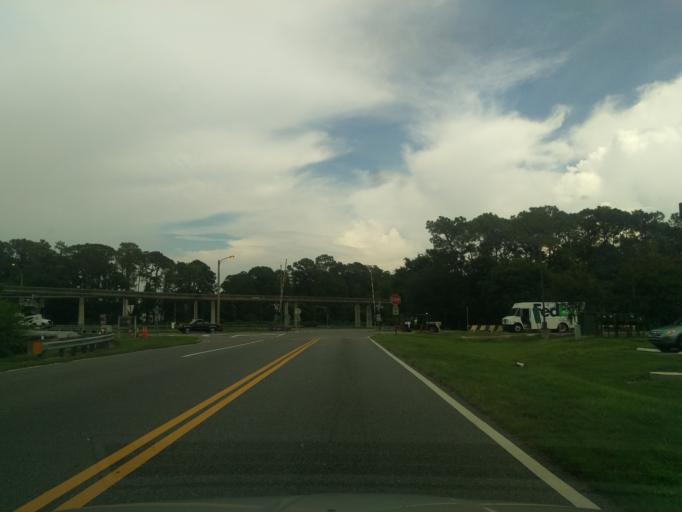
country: US
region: Florida
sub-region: Orange County
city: Bay Hill
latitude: 28.4238
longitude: -81.5799
